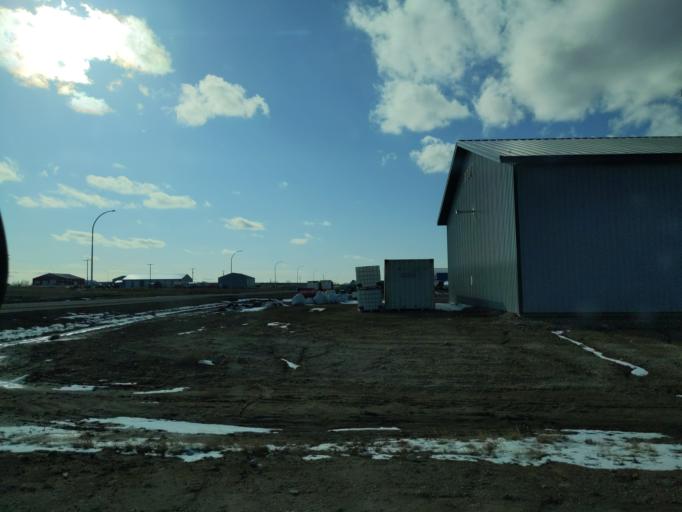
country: CA
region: Saskatchewan
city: Lloydminster
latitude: 53.2441
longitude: -109.9708
